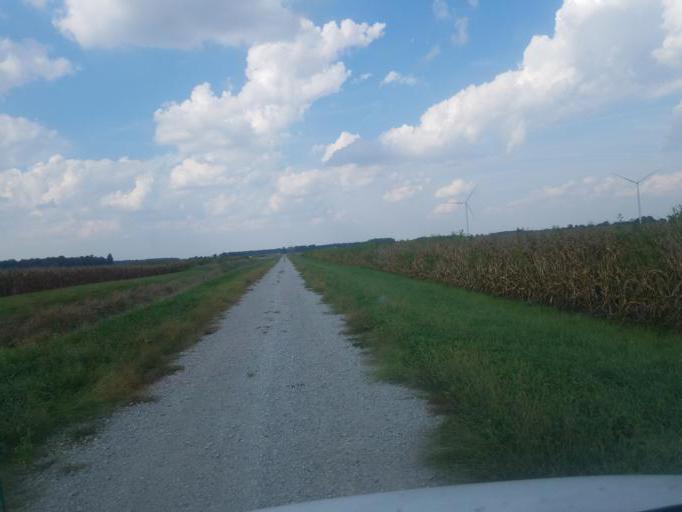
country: US
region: Ohio
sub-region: Hancock County
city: Arlington
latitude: 40.7935
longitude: -83.6899
